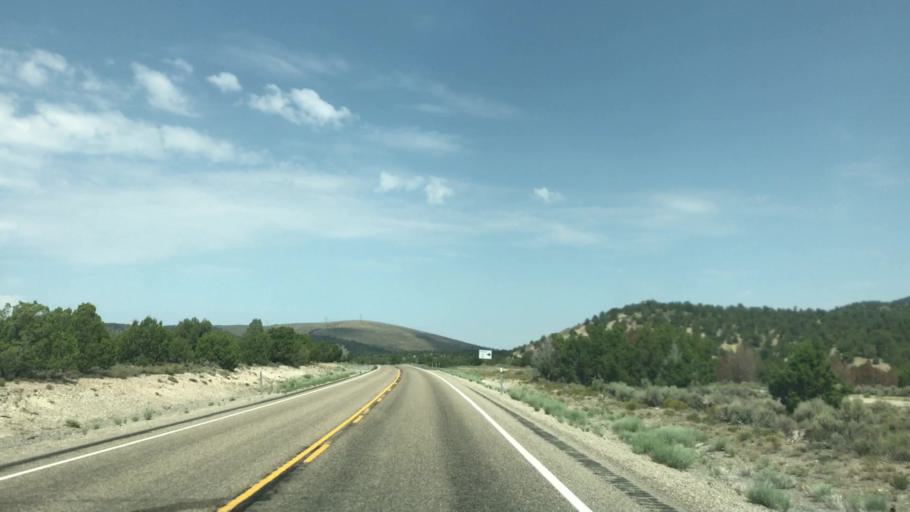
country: US
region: Nevada
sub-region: White Pine County
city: Ely
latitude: 39.3808
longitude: -115.0664
